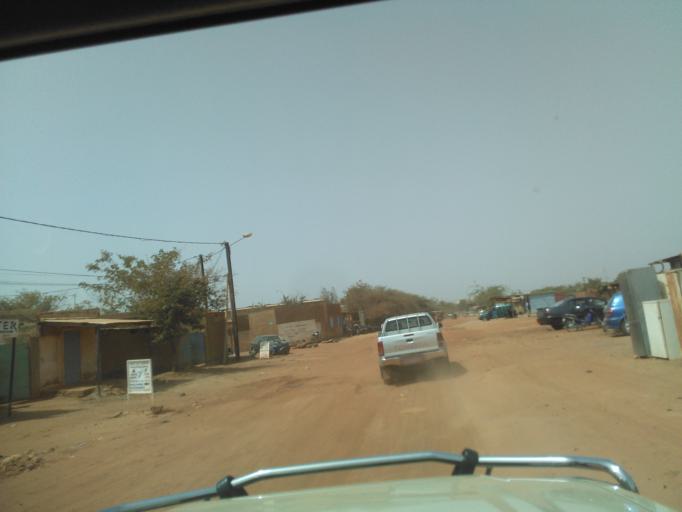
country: BF
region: Centre
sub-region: Kadiogo Province
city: Ouagadougou
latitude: 12.3812
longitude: -1.4777
